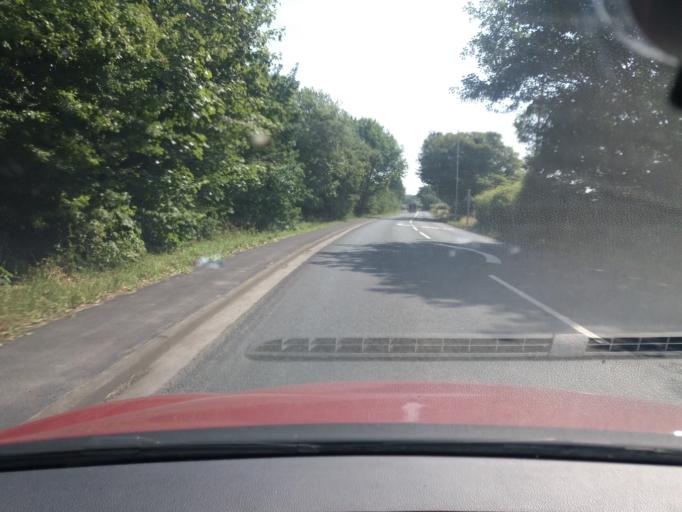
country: GB
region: England
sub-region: Lancashire
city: Euxton
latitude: 53.6439
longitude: -2.6784
